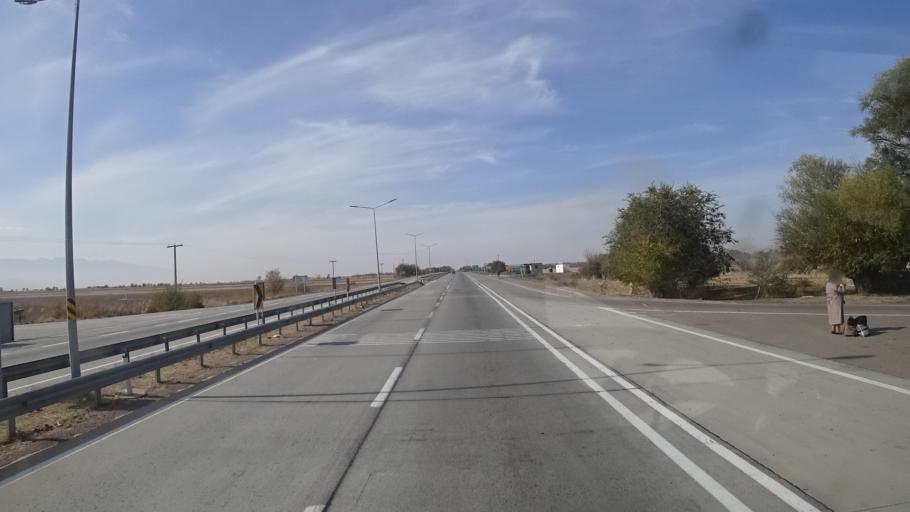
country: KZ
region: Zhambyl
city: Lugovoy
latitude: 42.9058
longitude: 72.9118
